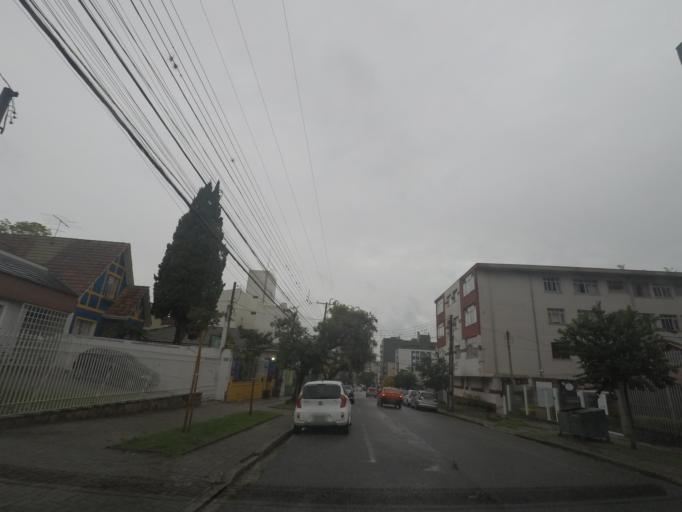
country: BR
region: Parana
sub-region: Curitiba
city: Curitiba
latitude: -25.4246
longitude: -49.2851
